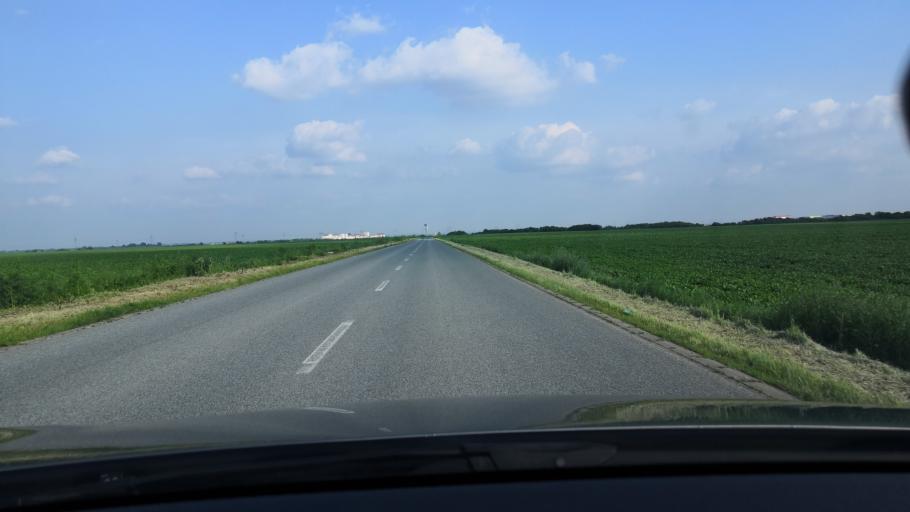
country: RS
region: Autonomna Pokrajina Vojvodina
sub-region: Sremski Okrug
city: Ingija
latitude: 45.0800
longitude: 20.1188
